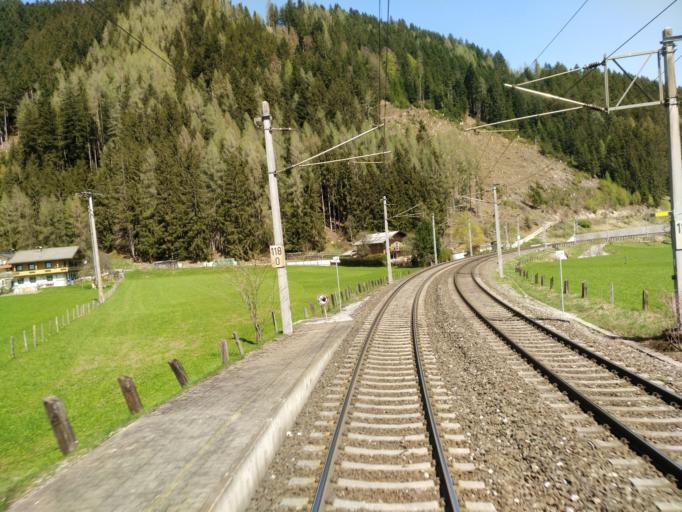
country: AT
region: Salzburg
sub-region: Politischer Bezirk Zell am See
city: Leogang
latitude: 47.4460
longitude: 12.7696
